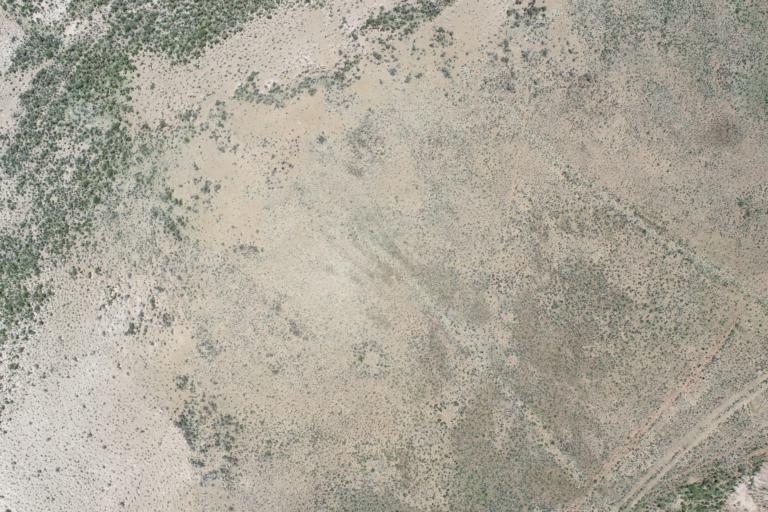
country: BO
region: La Paz
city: Curahuara de Carangas
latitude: -17.3070
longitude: -68.5047
